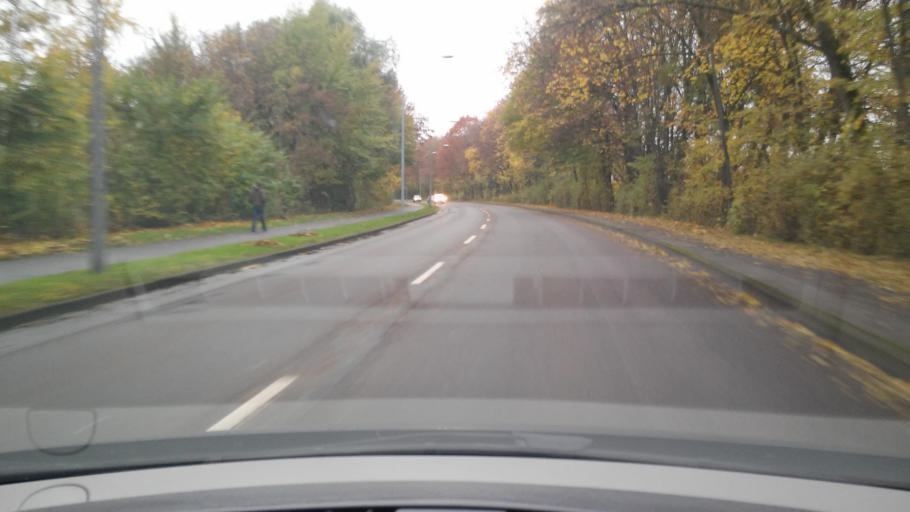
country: DE
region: Saarland
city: Saarlouis
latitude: 49.3157
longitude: 6.7590
